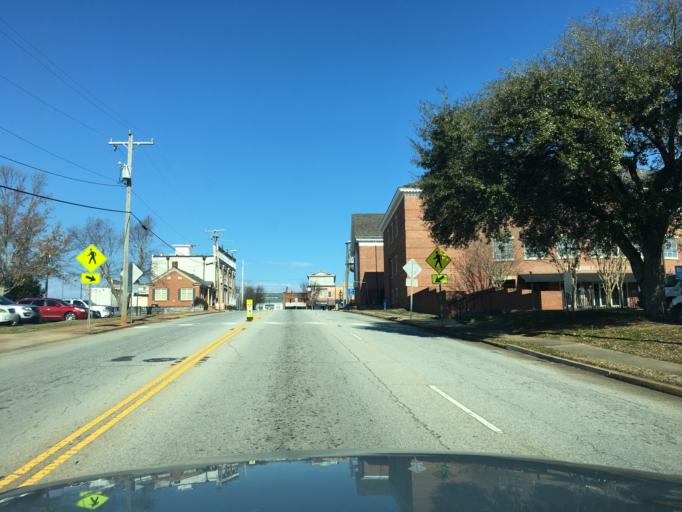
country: US
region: South Carolina
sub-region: Pickens County
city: Pickens
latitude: 34.8826
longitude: -82.7068
